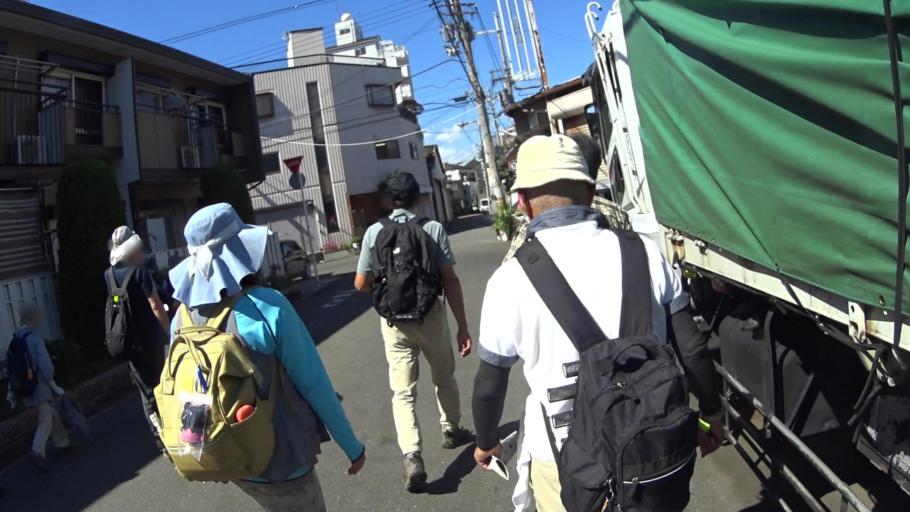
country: JP
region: Osaka
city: Yao
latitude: 34.6345
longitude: 135.5515
